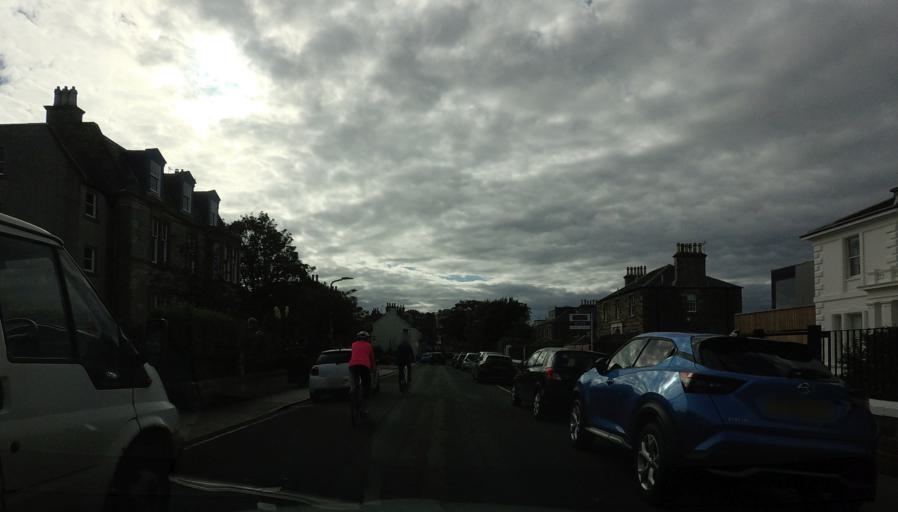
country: GB
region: Scotland
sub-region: East Lothian
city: North Berwick
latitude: 56.0581
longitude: -2.7236
